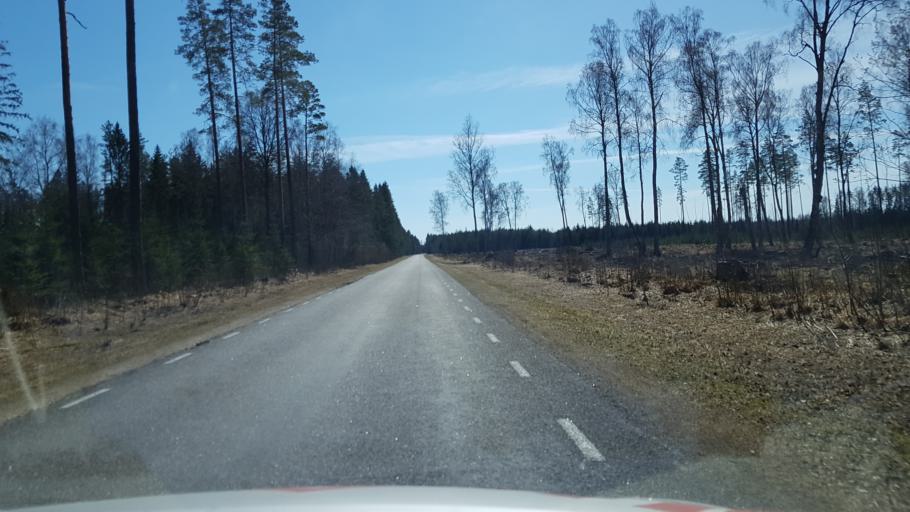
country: EE
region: Laeaene-Virumaa
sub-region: Vinni vald
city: Vinni
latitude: 59.1487
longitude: 26.5198
